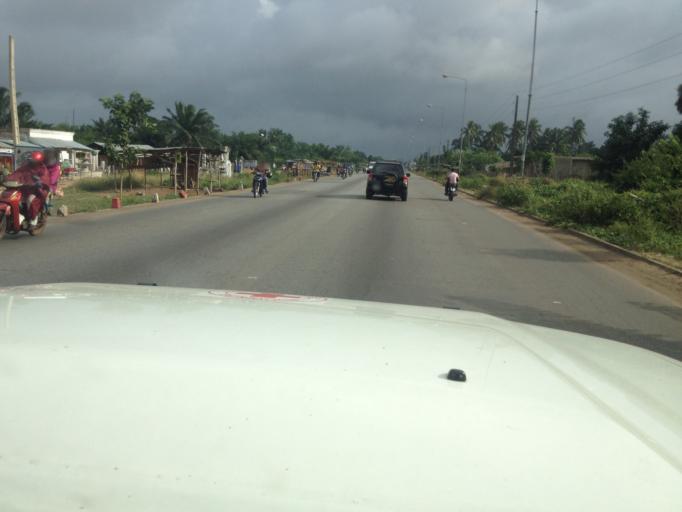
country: BJ
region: Queme
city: Porto-Novo
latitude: 6.4392
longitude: 2.6234
